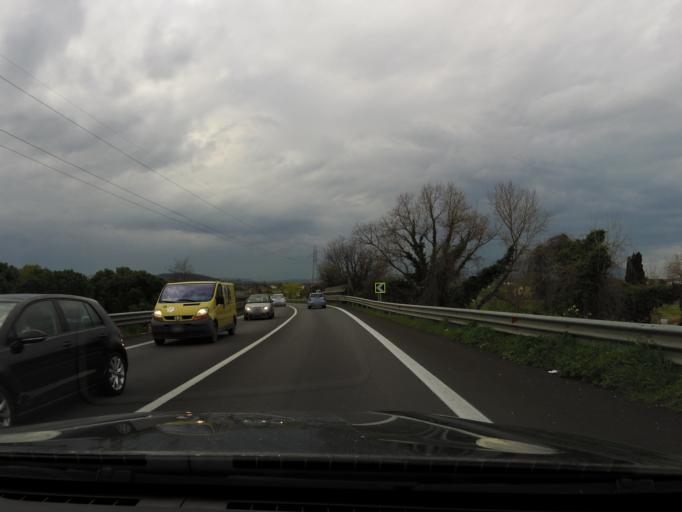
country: IT
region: The Marches
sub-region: Provincia di Ancona
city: Loreto Stazione
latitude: 43.4434
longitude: 13.6347
